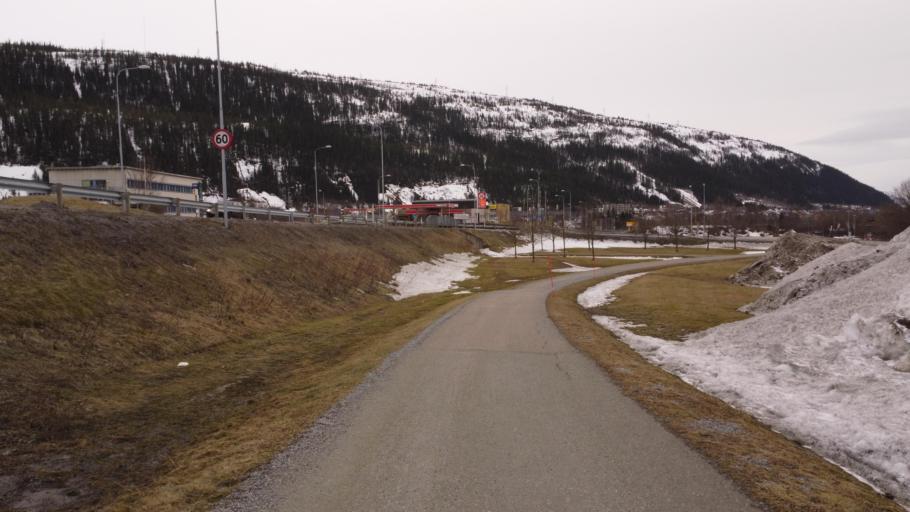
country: NO
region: Nordland
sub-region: Rana
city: Mo i Rana
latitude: 66.3088
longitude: 14.1521
